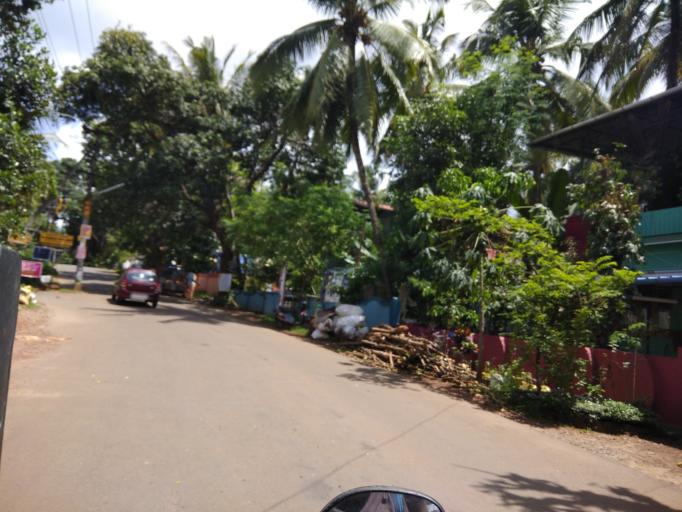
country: IN
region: Kerala
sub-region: Thrissur District
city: Avanoor
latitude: 10.5499
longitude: 76.1489
